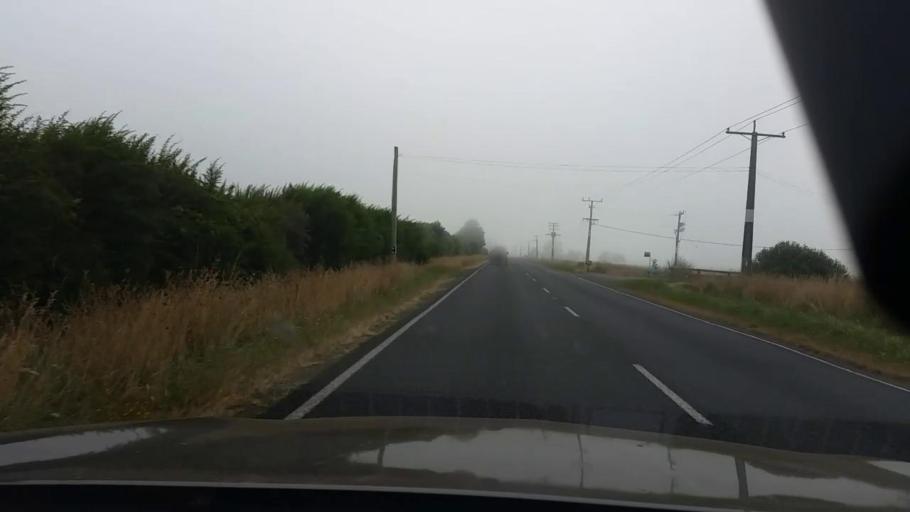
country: NZ
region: Waikato
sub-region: Hamilton City
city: Hamilton
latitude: -37.6356
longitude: 175.3017
